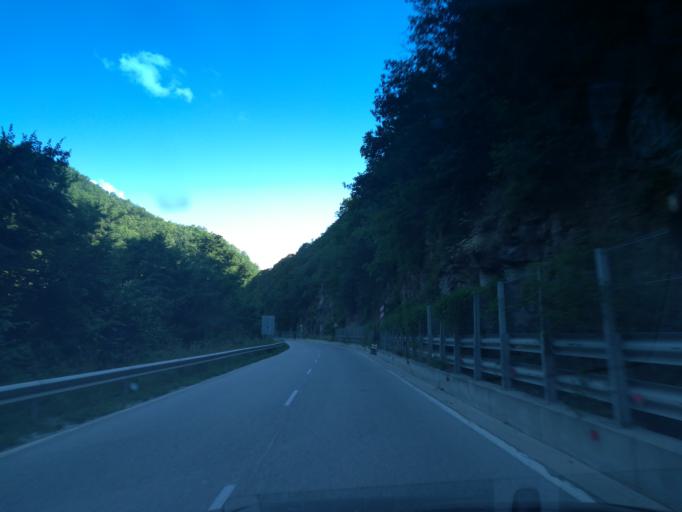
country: BG
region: Smolyan
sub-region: Obshtina Chepelare
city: Chepelare
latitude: 41.8015
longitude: 24.7097
